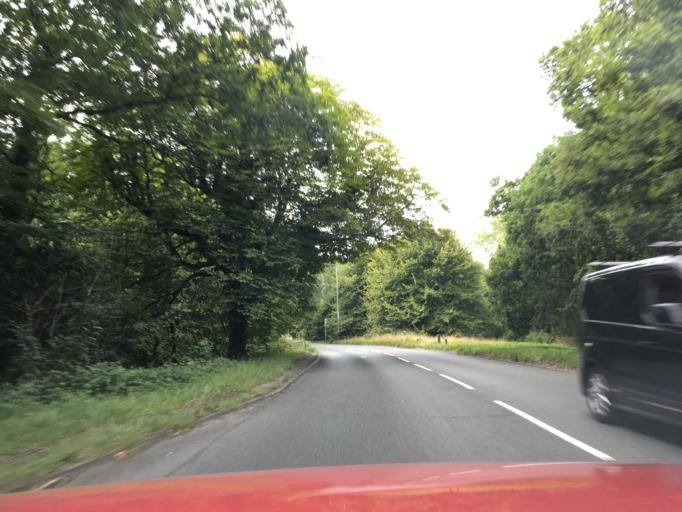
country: GB
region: England
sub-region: Kent
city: Royal Tunbridge Wells
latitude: 51.1320
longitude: 0.2382
